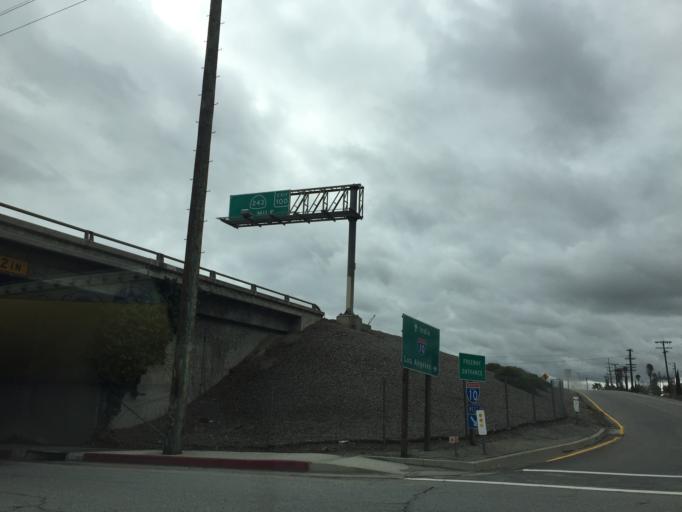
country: US
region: California
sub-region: Riverside County
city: Banning
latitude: 33.9246
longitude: -116.8679
